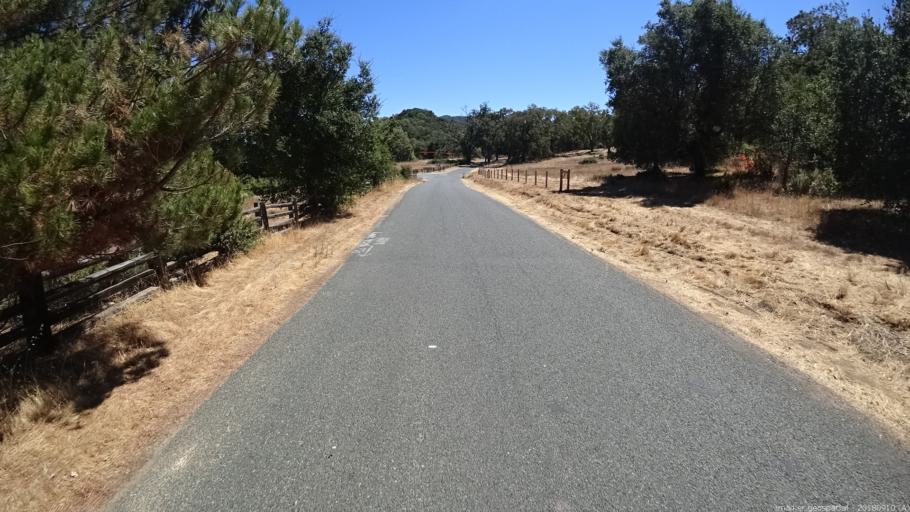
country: US
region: California
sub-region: Monterey County
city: Carmel Valley Village
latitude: 36.4391
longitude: -121.7958
